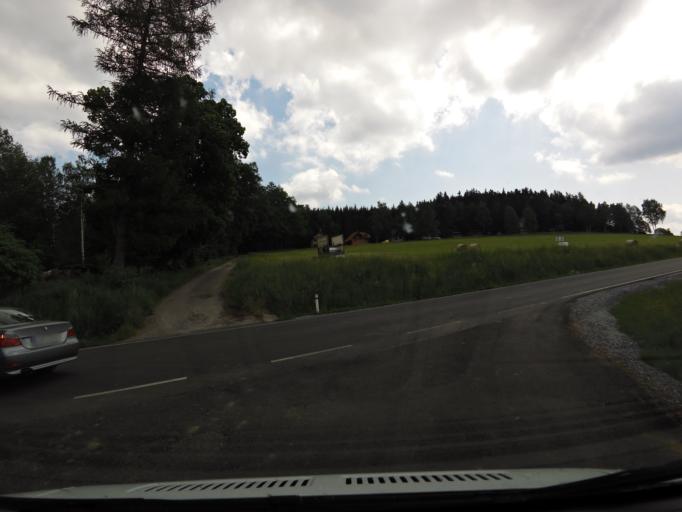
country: CZ
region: Jihocesky
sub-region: Okres Cesky Krumlov
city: Horni Plana
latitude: 48.7756
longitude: 14.0191
